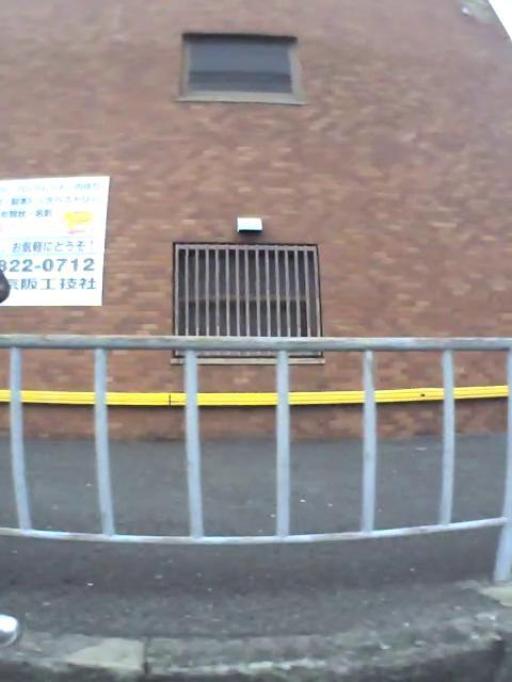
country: JP
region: Osaka
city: Neyagawa
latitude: 34.7607
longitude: 135.6281
